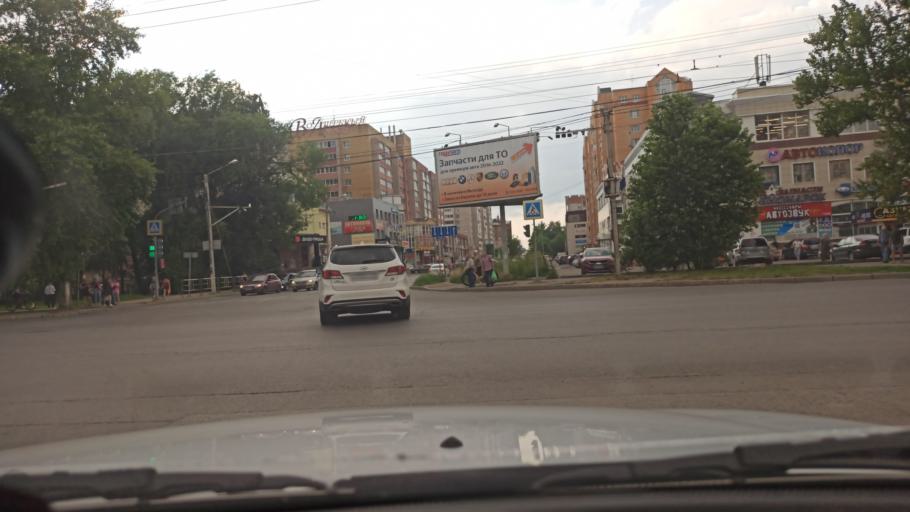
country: RU
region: Vologda
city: Vologda
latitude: 59.2086
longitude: 39.8450
